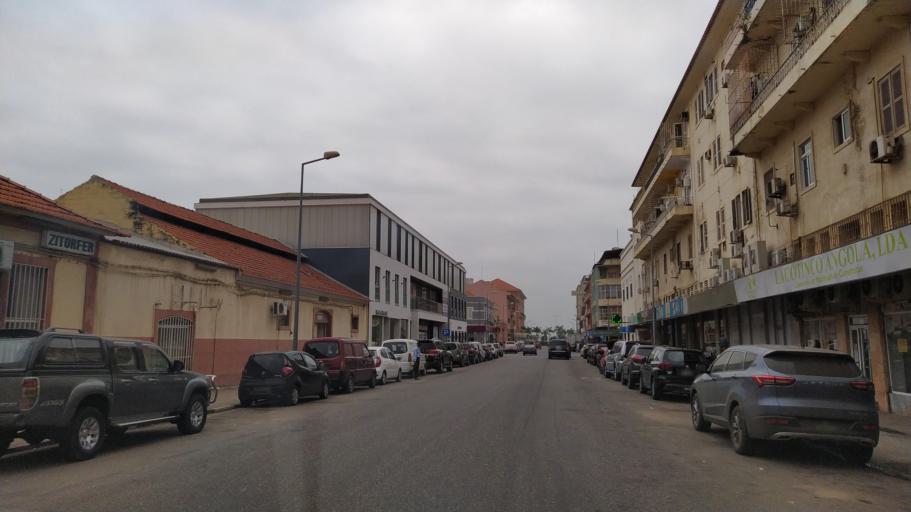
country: AO
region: Luanda
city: Luanda
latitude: -8.8126
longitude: 13.2348
